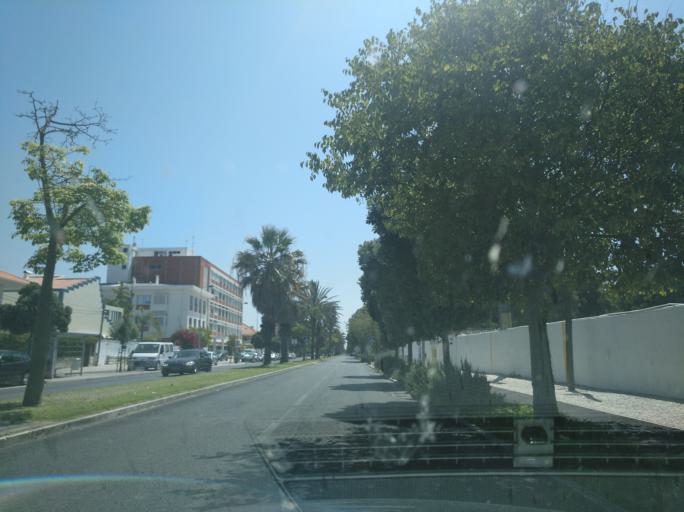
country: PT
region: Setubal
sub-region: Almada
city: Trafaria
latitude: 38.6630
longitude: -9.2432
